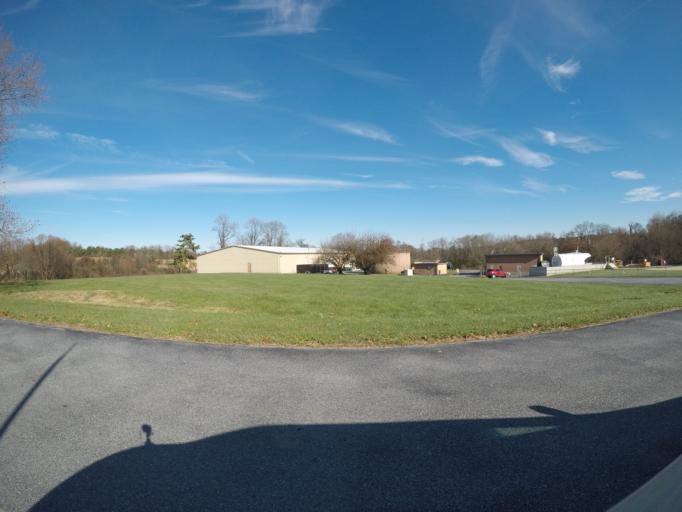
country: US
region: Pennsylvania
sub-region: Chester County
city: Caln
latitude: 40.0104
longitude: -75.7850
